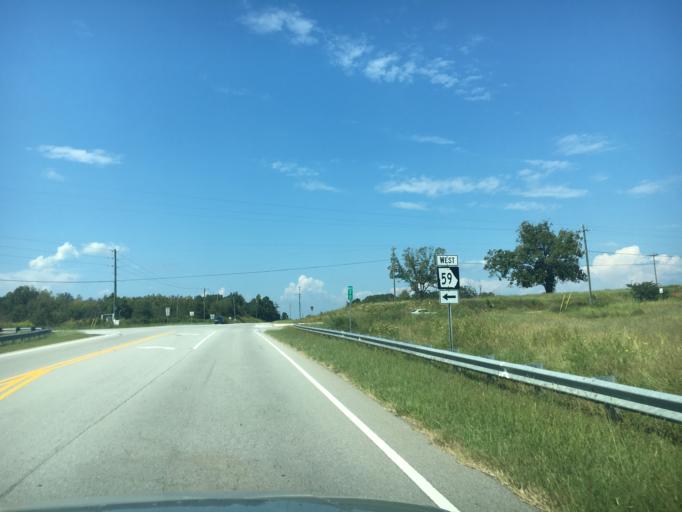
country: US
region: Georgia
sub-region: Franklin County
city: Gumlog
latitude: 34.4675
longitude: -83.0588
